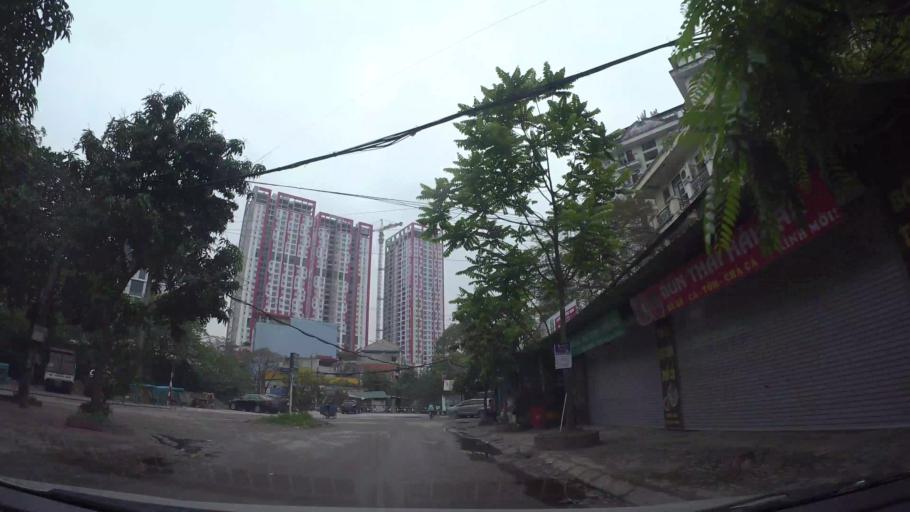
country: VN
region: Ha Noi
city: Cau Giay
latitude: 21.0324
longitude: 105.7844
